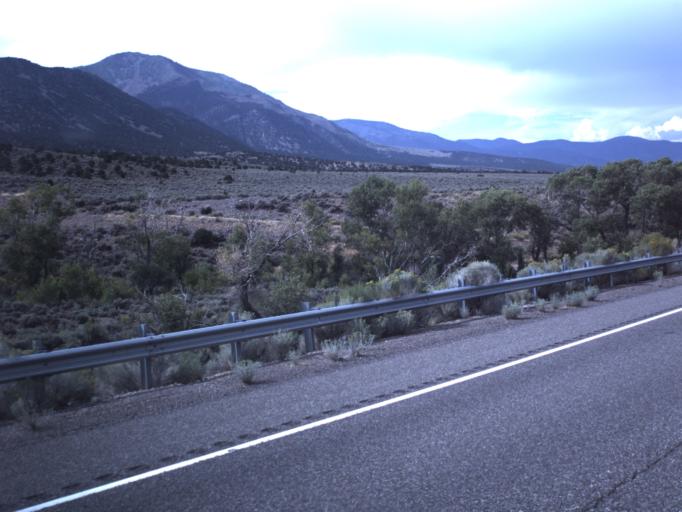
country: US
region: Utah
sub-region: Piute County
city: Junction
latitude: 38.3439
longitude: -112.2183
